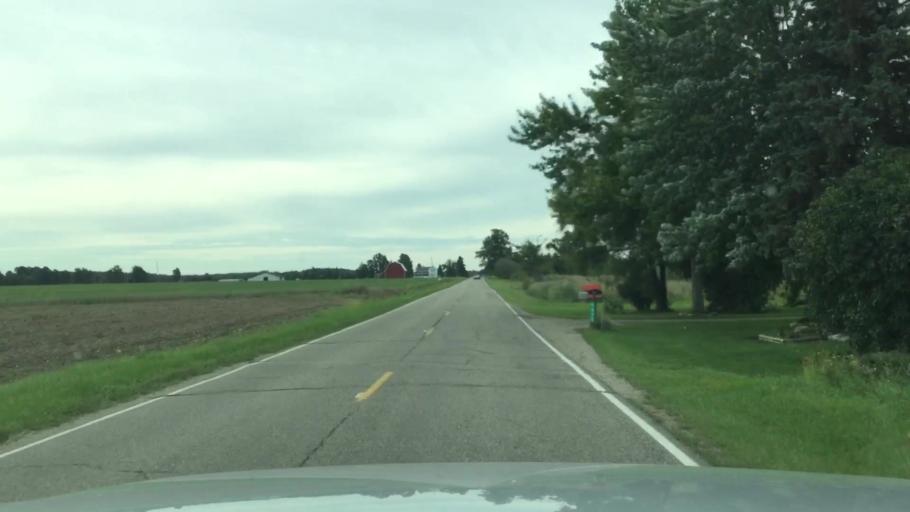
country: US
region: Michigan
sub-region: Genesee County
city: Montrose
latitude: 43.0841
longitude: -83.9877
